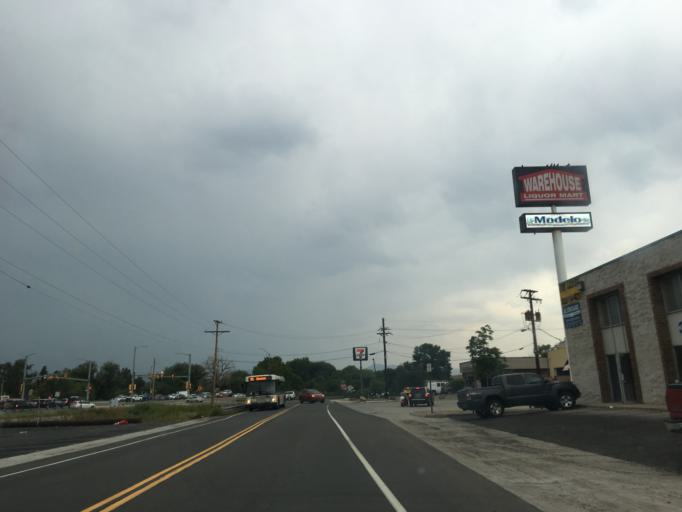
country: US
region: Colorado
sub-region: Arapahoe County
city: Sheridan
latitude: 39.6533
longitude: -105.0306
